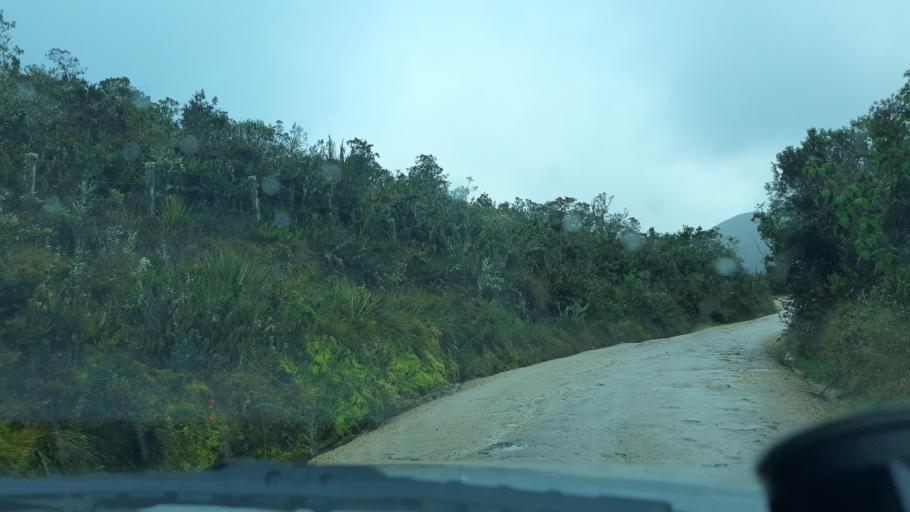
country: CO
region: Cundinamarca
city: Villapinzon
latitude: 5.2168
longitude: -73.5337
